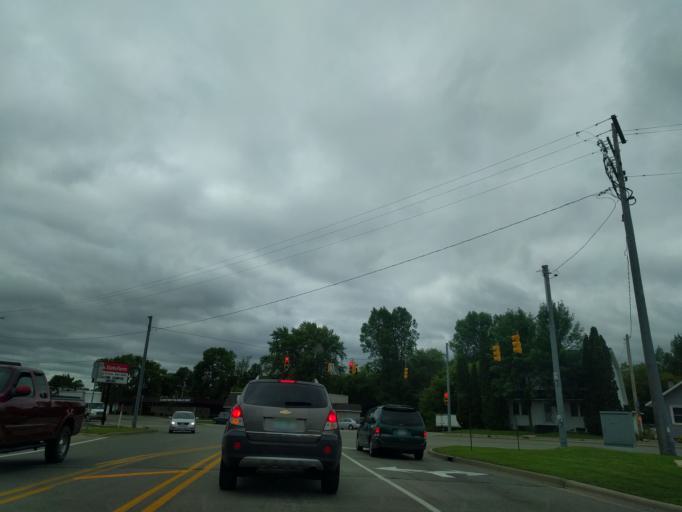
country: US
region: Michigan
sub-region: Menominee County
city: Menominee
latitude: 45.1346
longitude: -87.6120
